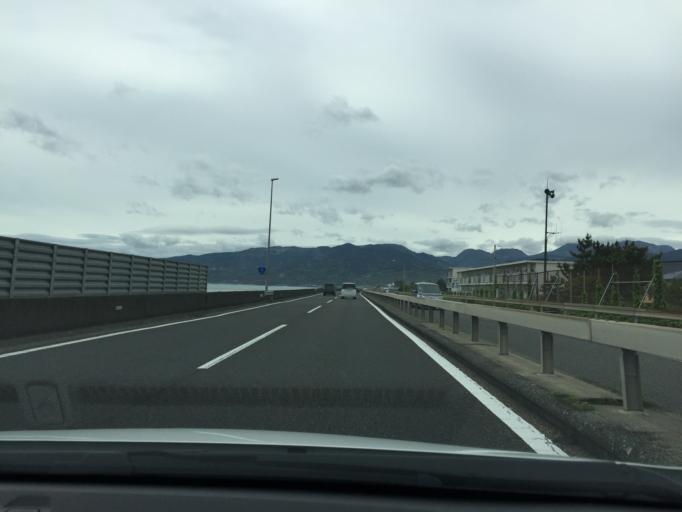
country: JP
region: Kanagawa
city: Odawara
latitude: 35.2656
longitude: 139.1920
